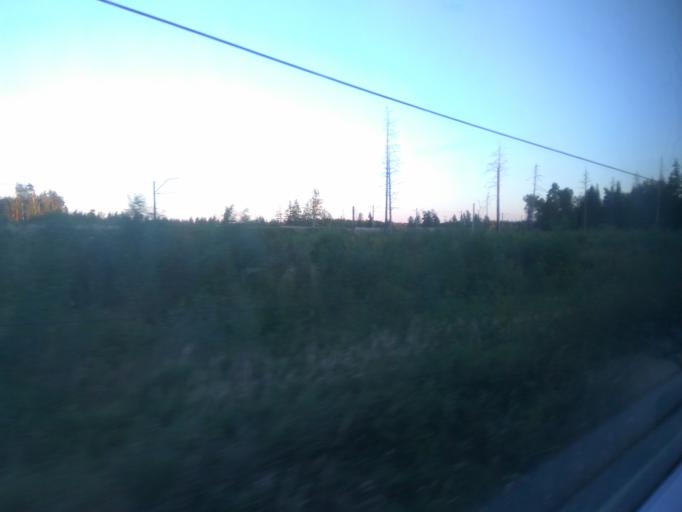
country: RU
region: Moskovskaya
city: Fryazevo
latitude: 55.7410
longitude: 38.4795
